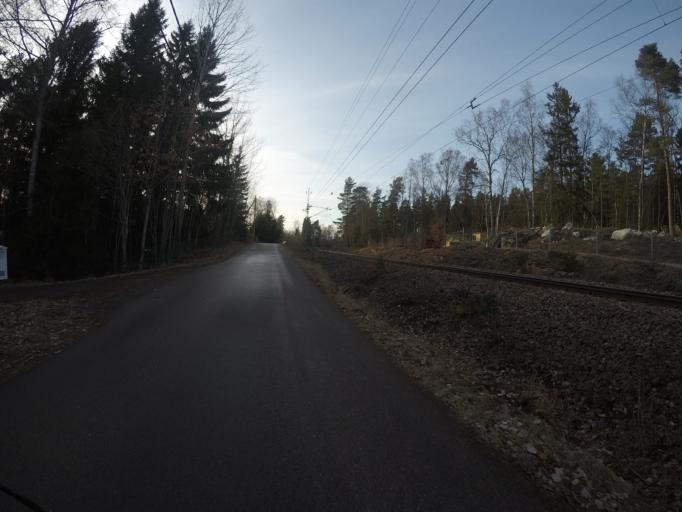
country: SE
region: Soedermanland
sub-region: Eskilstuna Kommun
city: Kvicksund
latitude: 59.4598
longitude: 16.3029
